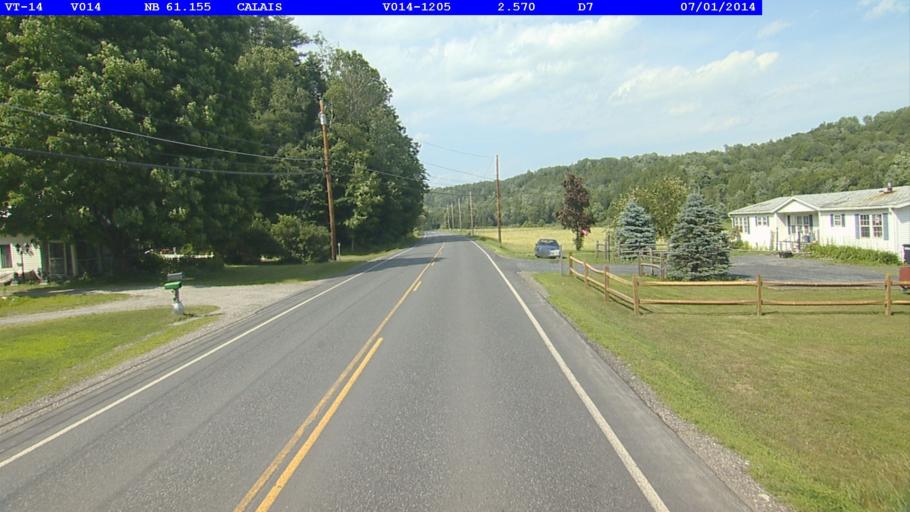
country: US
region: Vermont
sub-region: Washington County
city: Montpelier
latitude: 44.3433
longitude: -72.4426
